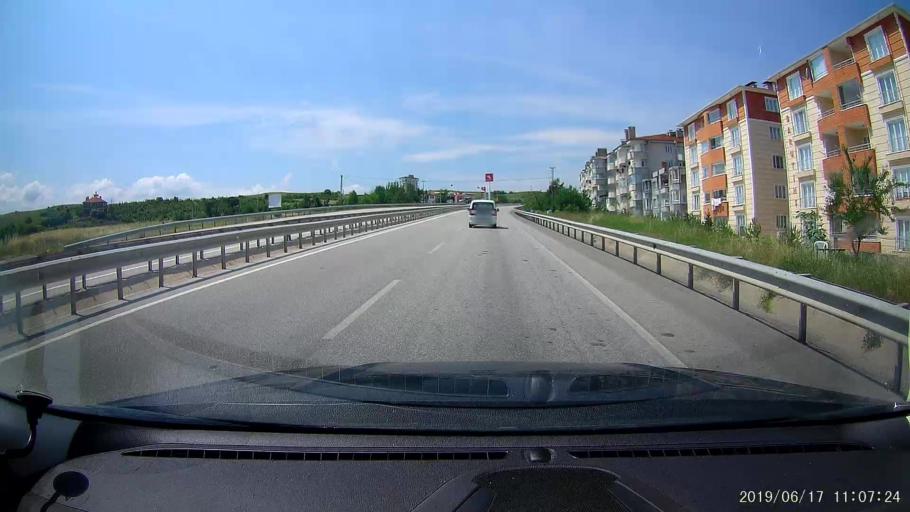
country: TR
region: Kastamonu
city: Tosya
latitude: 41.0029
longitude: 34.0549
